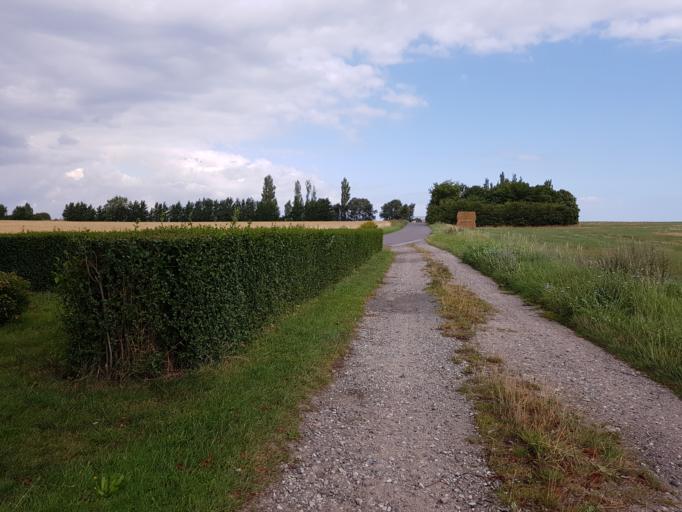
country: DK
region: Zealand
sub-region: Guldborgsund Kommune
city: Nykobing Falster
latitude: 54.5817
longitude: 11.9436
